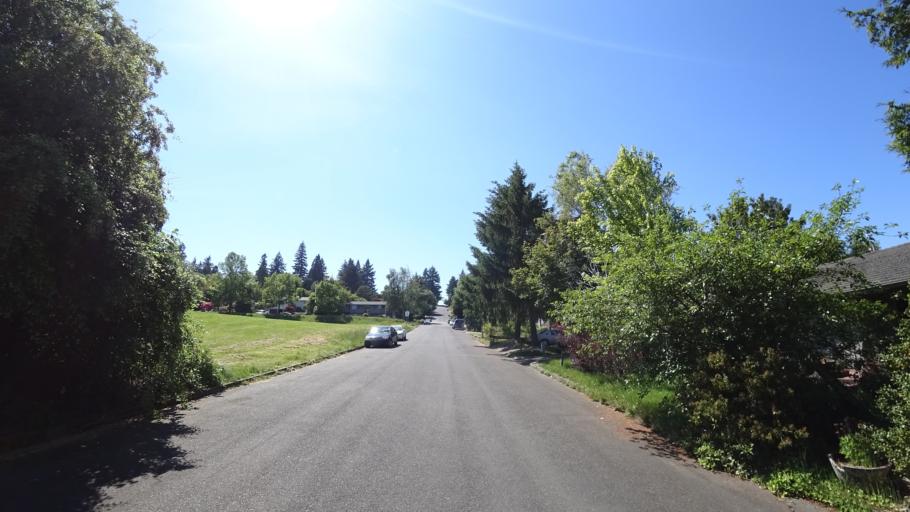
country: US
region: Oregon
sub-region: Washington County
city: Metzger
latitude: 45.4511
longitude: -122.7167
